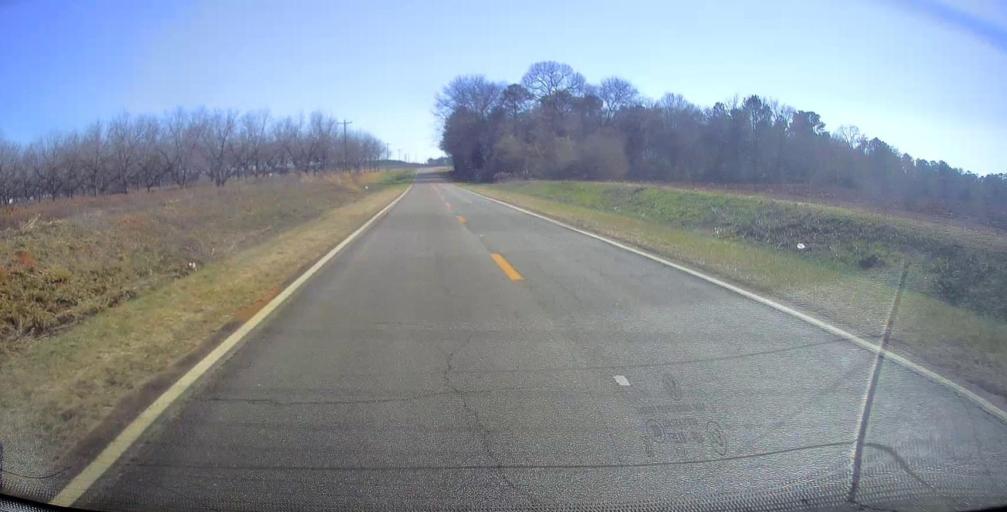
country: US
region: Georgia
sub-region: Crawford County
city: Knoxville
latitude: 32.6151
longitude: -83.9848
